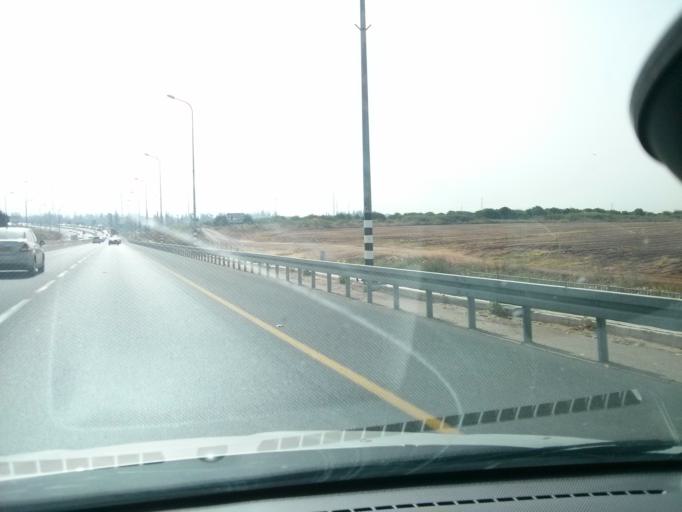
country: IL
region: Central District
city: Even Yehuda
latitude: 32.2551
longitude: 34.8812
